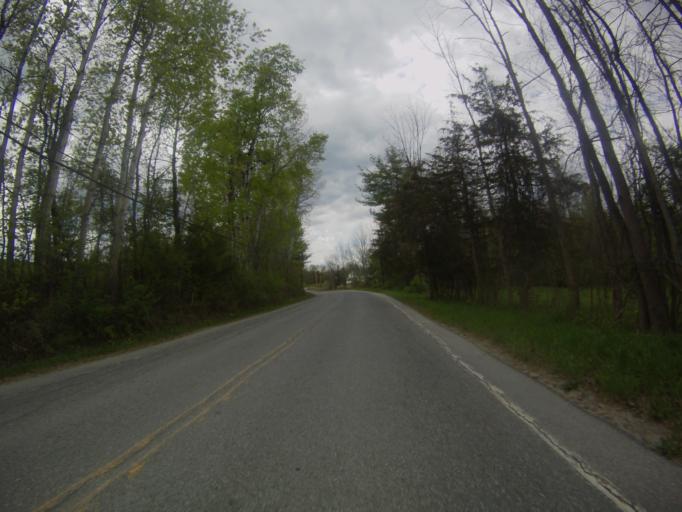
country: US
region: New York
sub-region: Essex County
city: Port Henry
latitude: 43.9504
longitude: -73.4768
